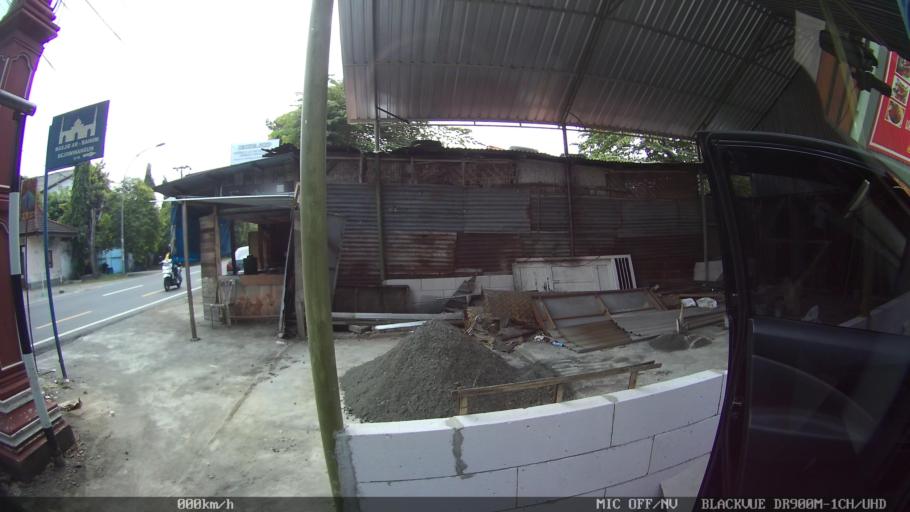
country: ID
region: Daerah Istimewa Yogyakarta
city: Yogyakarta
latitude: -7.8130
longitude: 110.3963
